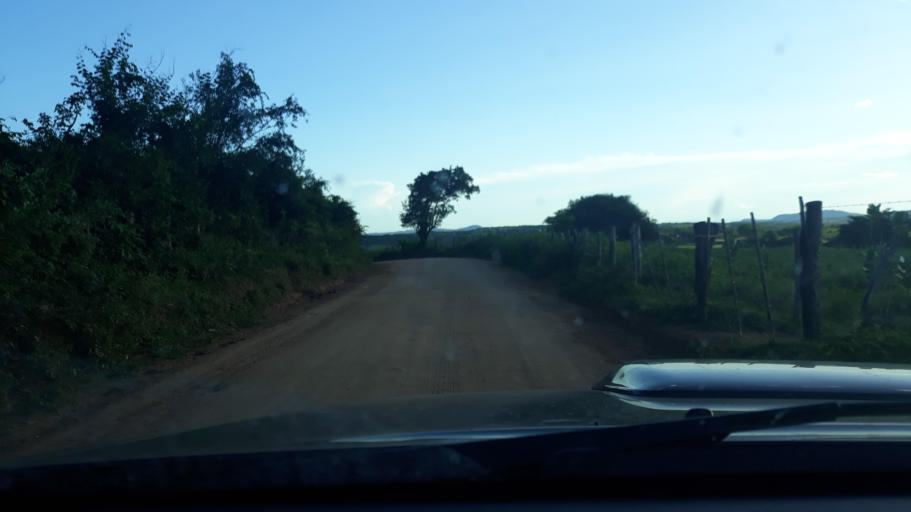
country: BR
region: Bahia
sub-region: Riacho De Santana
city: Riacho de Santana
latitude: -13.8189
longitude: -42.7240
